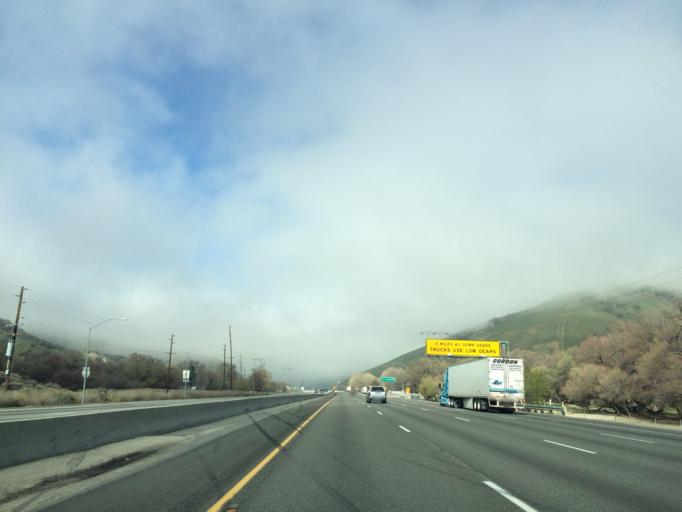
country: US
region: California
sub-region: Kern County
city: Lebec
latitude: 34.8717
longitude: -118.8890
